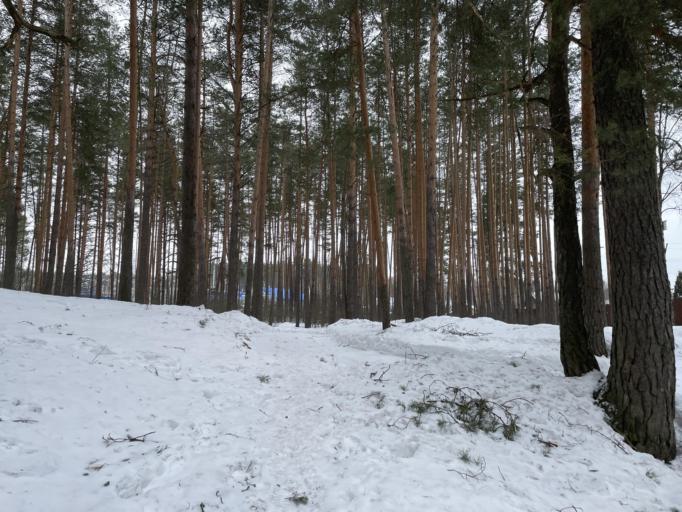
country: RU
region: Vladimir
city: Pokrov
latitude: 55.9380
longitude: 39.2373
